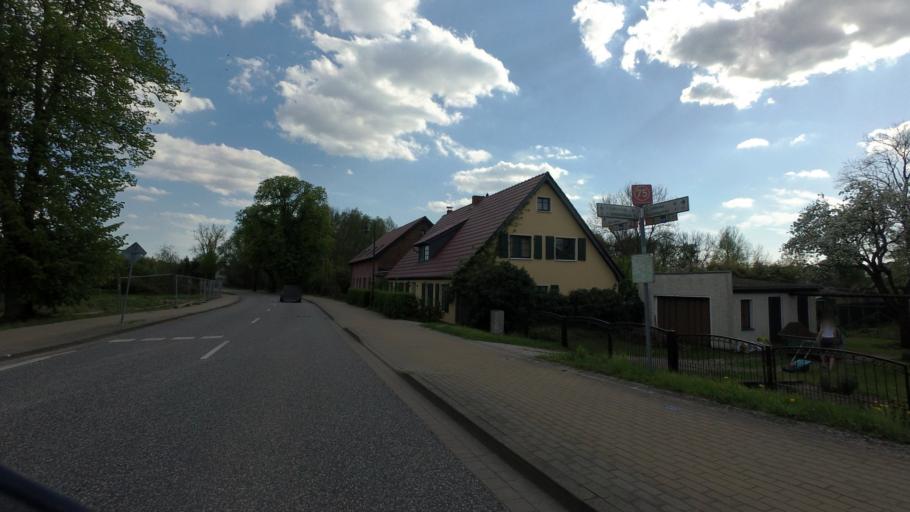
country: DE
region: Brandenburg
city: Liebenwalde
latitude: 52.8651
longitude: 13.3966
